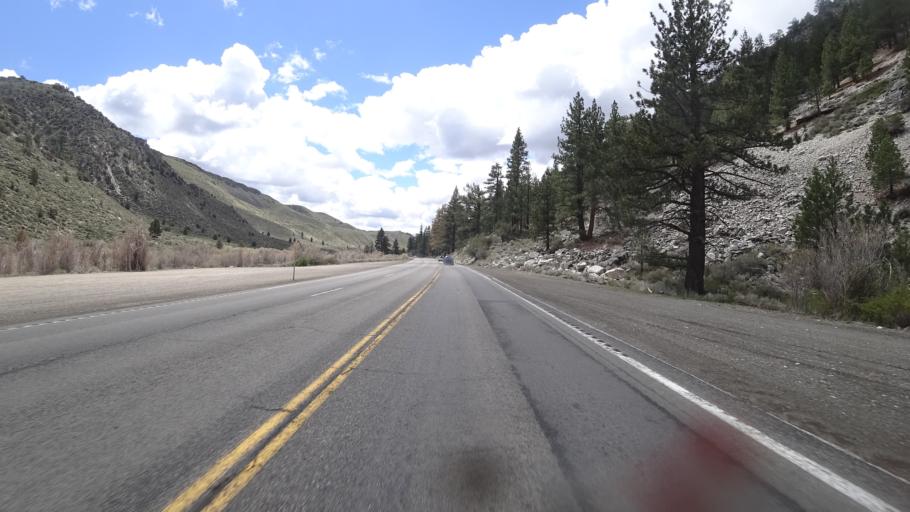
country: US
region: California
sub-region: Mono County
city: Bridgeport
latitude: 38.4027
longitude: -119.4535
